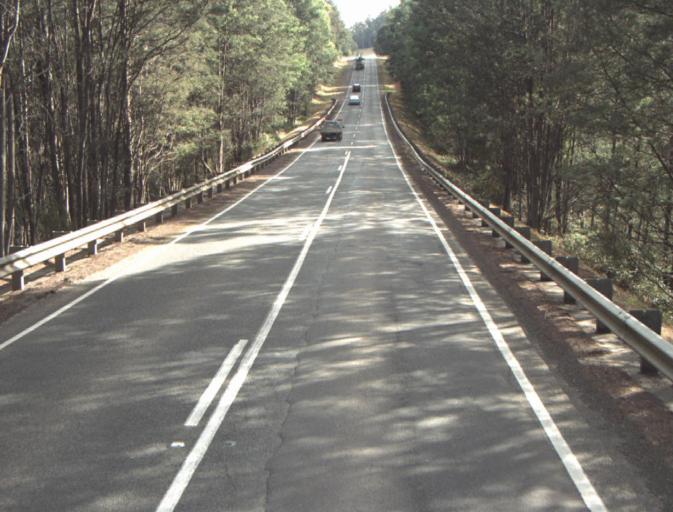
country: AU
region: Tasmania
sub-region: Launceston
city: Mayfield
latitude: -41.2959
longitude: 147.2133
